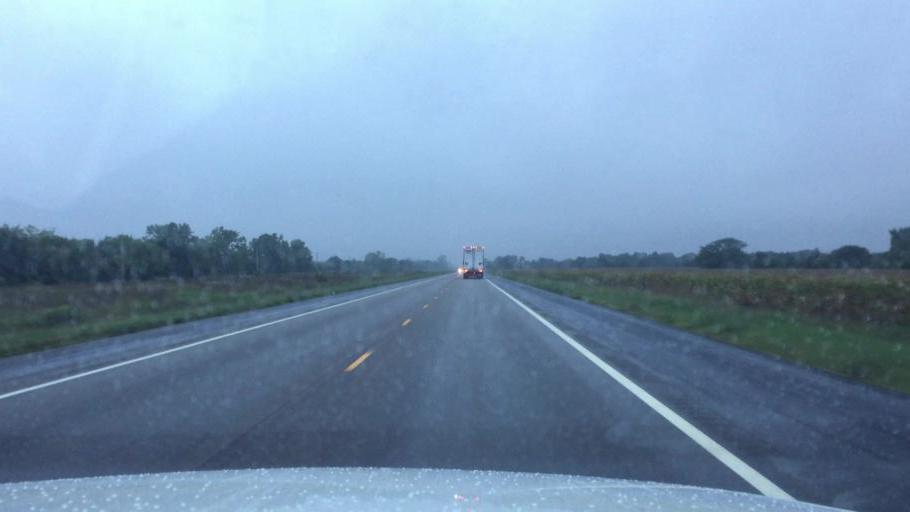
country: US
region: Kansas
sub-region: Montgomery County
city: Cherryvale
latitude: 37.4030
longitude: -95.5026
